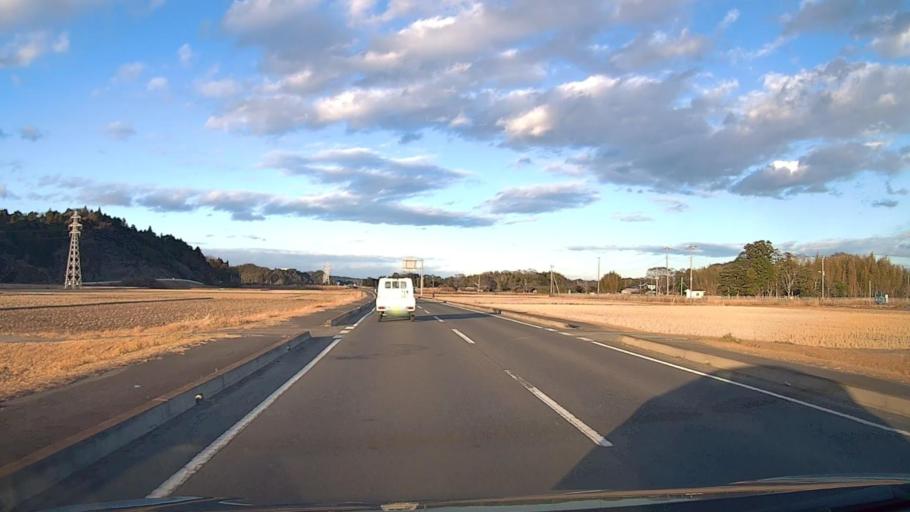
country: JP
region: Ibaraki
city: Kitaibaraki
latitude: 36.8238
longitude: 140.7653
